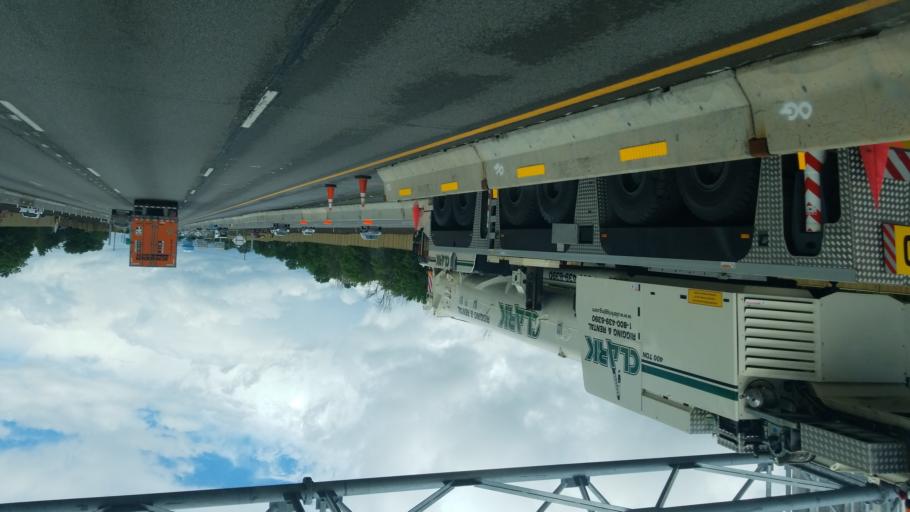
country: US
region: New York
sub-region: Erie County
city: Cheektowaga
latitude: 42.9364
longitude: -78.7662
